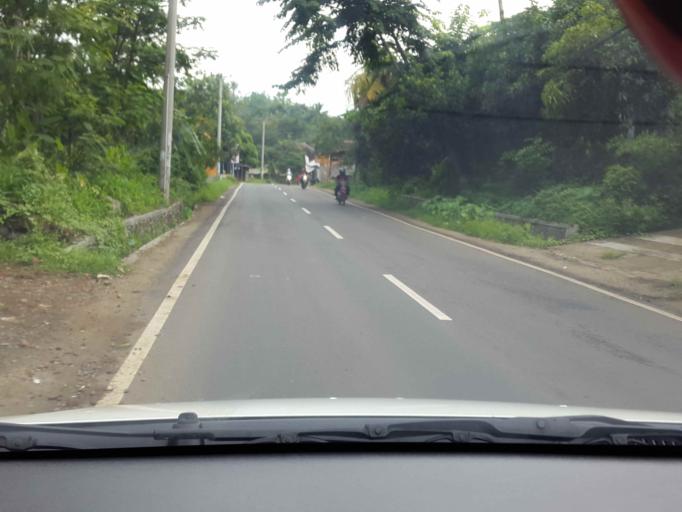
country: ID
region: West Java
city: Cidadap
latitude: -7.0225
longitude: 106.5633
